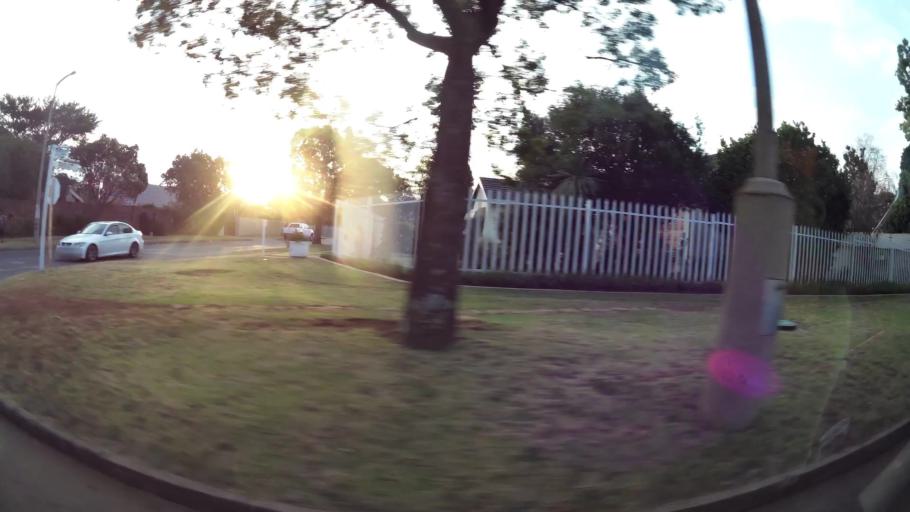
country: ZA
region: Gauteng
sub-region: Ekurhuleni Metropolitan Municipality
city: Benoni
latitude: -26.1695
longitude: 28.3009
